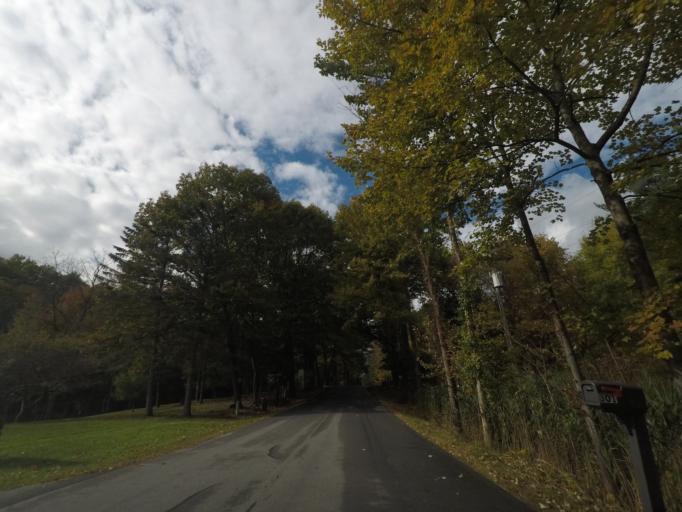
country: US
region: New York
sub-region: Rensselaer County
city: East Greenbush
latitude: 42.5808
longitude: -73.6493
